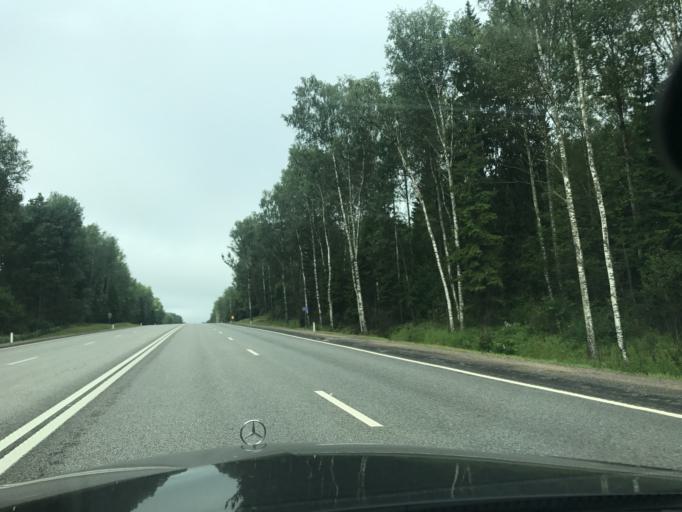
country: RU
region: Smolensk
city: Vyaz'ma
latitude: 55.3085
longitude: 34.5124
